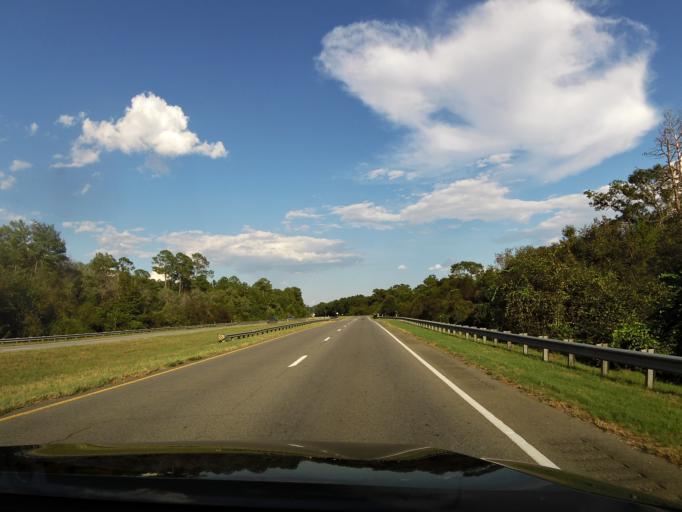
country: US
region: Georgia
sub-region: Brooks County
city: Quitman
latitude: 30.7864
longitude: -83.5181
